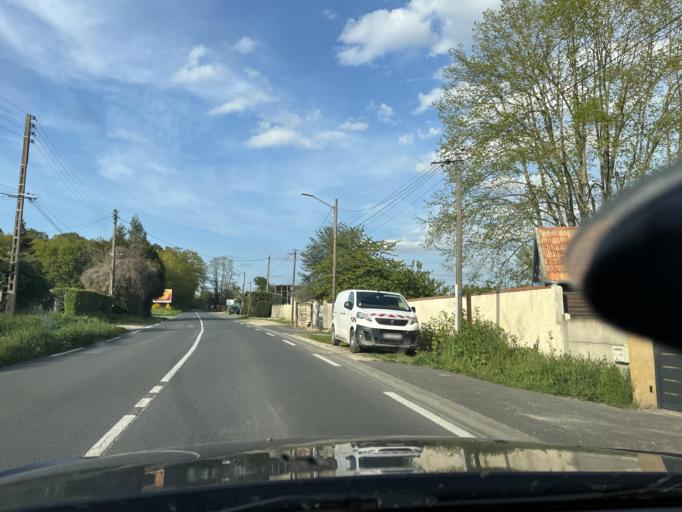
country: FR
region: Ile-de-France
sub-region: Departement de l'Essonne
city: Breuillet
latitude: 48.5600
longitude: 2.1527
